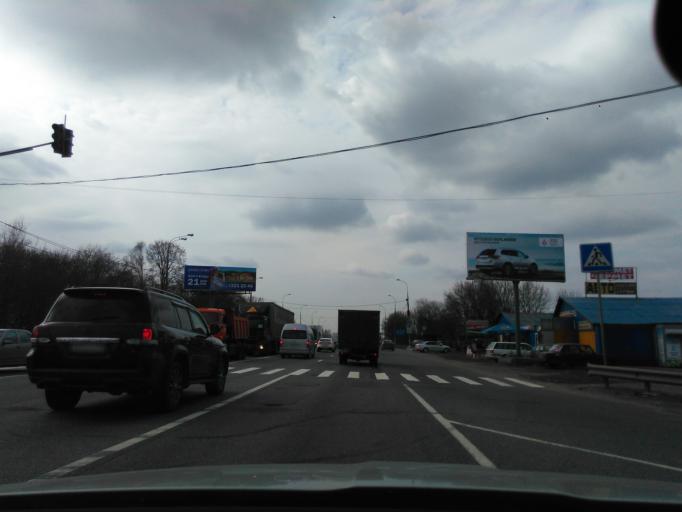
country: RU
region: Moskovskaya
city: Sheremet'yevskiy
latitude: 55.9938
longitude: 37.5338
